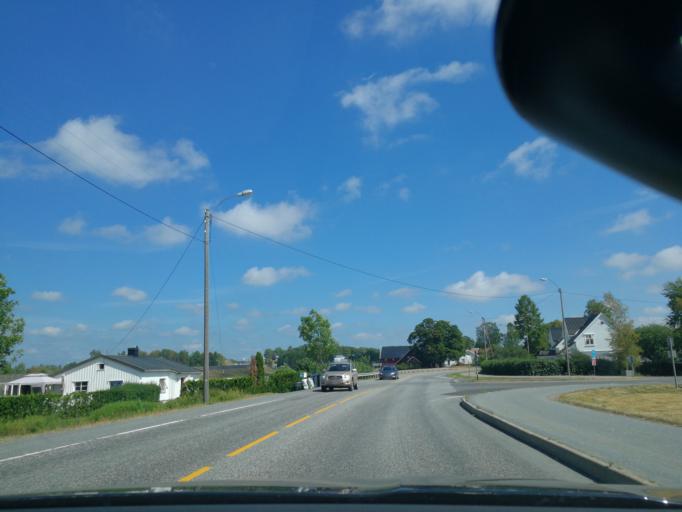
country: NO
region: Vestfold
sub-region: Sandefjord
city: Sandefjord
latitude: 59.1648
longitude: 10.2033
